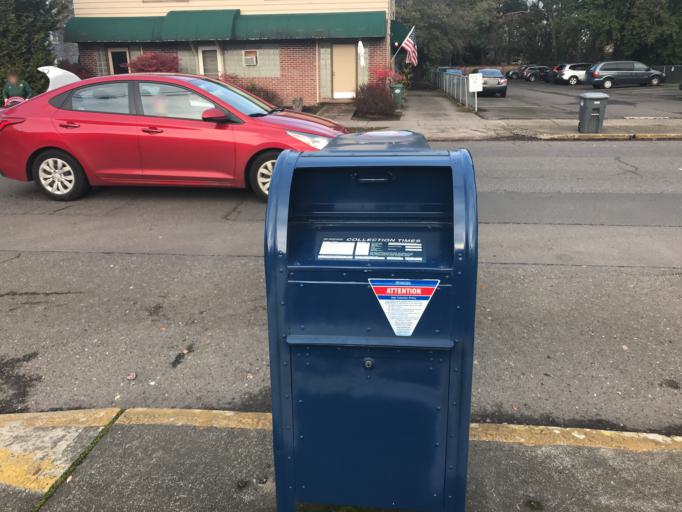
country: US
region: Oregon
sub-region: Washington County
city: Hillsboro
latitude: 45.5238
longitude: -122.9871
